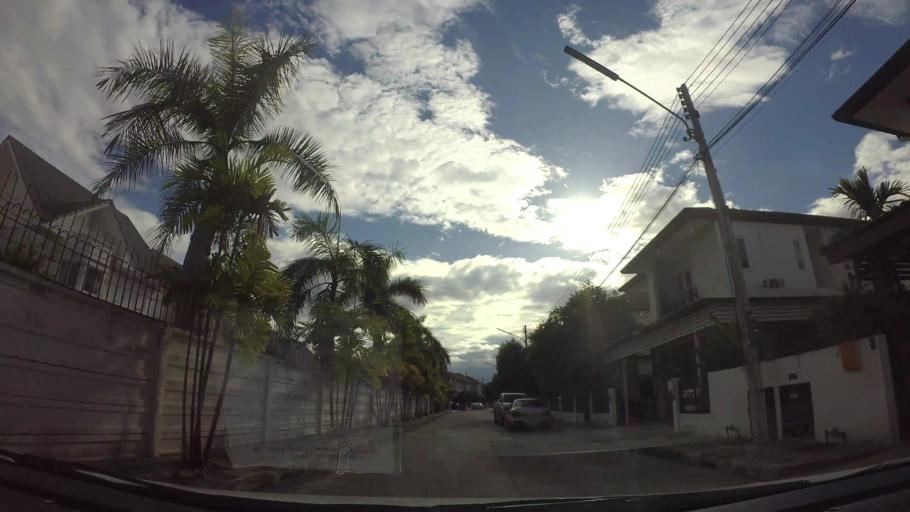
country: TH
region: Chiang Mai
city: Saraphi
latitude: 18.7529
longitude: 99.0276
